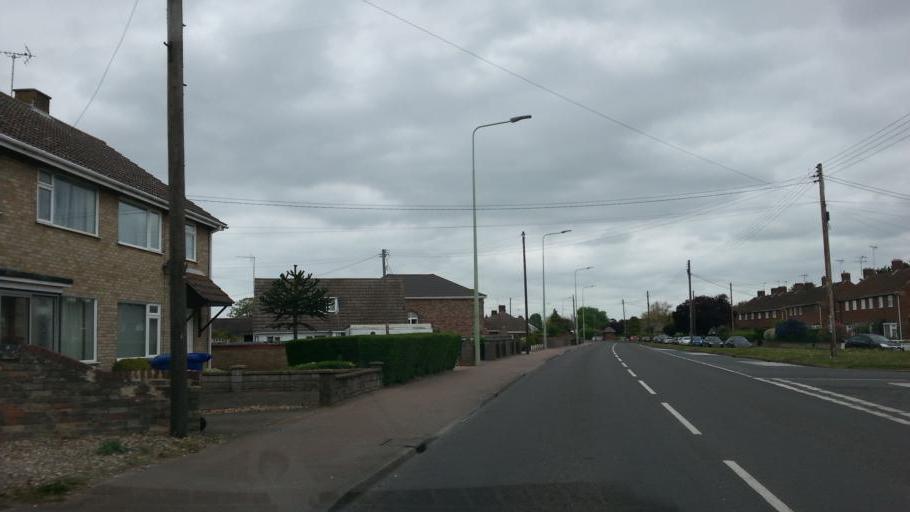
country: GB
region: England
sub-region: Suffolk
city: Lakenheath
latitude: 52.3483
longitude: 0.5110
